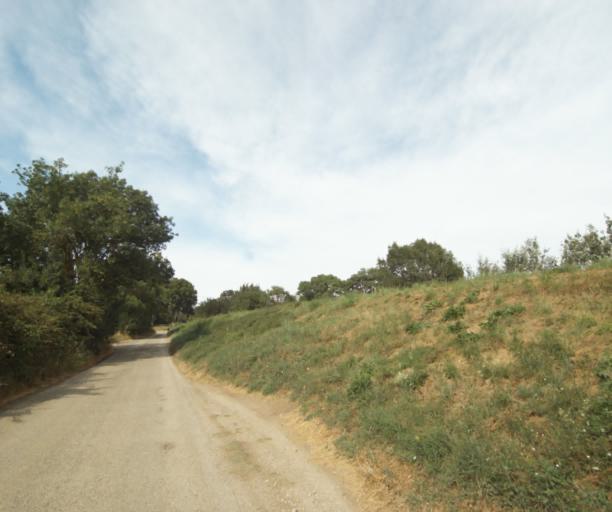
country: FR
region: Languedoc-Roussillon
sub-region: Departement de l'Herault
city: Marsillargues
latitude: 43.6379
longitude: 4.1891
